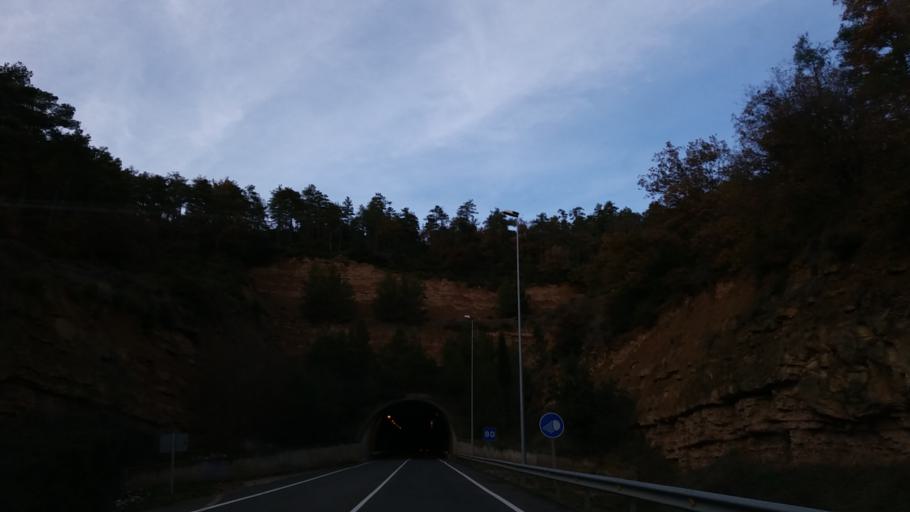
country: ES
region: Catalonia
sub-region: Provincia de Lleida
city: Tiurana
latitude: 41.9859
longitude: 1.2940
